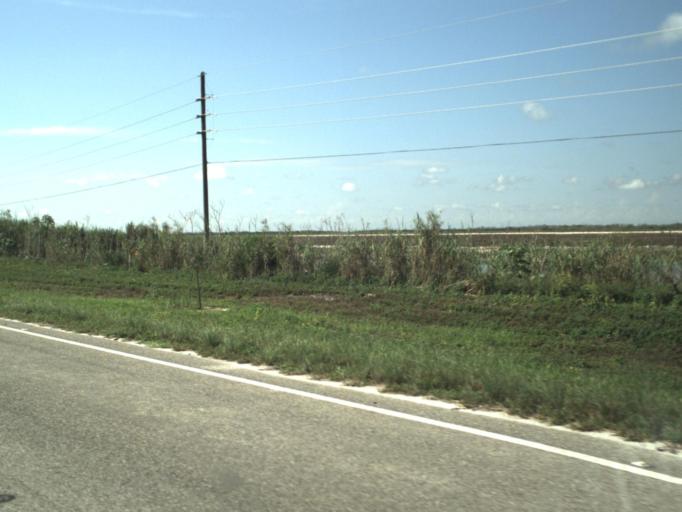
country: US
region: Florida
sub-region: Palm Beach County
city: Belle Glade Camp
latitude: 26.4248
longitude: -80.6076
